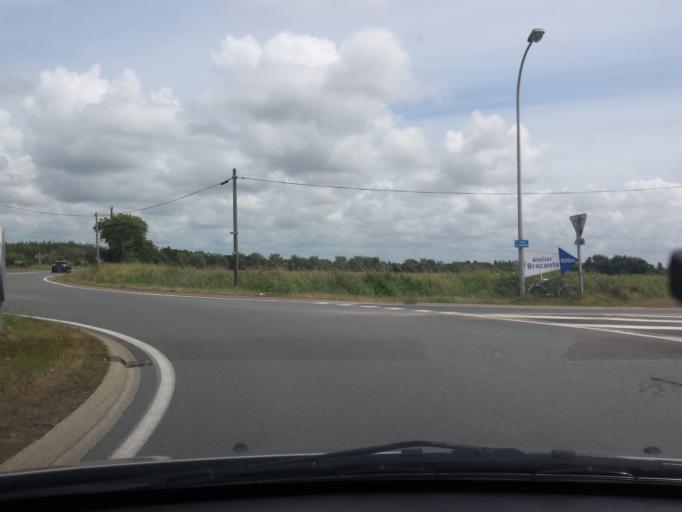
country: FR
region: Pays de la Loire
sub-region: Departement de la Vendee
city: Givrand
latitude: 46.6933
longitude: -1.8980
